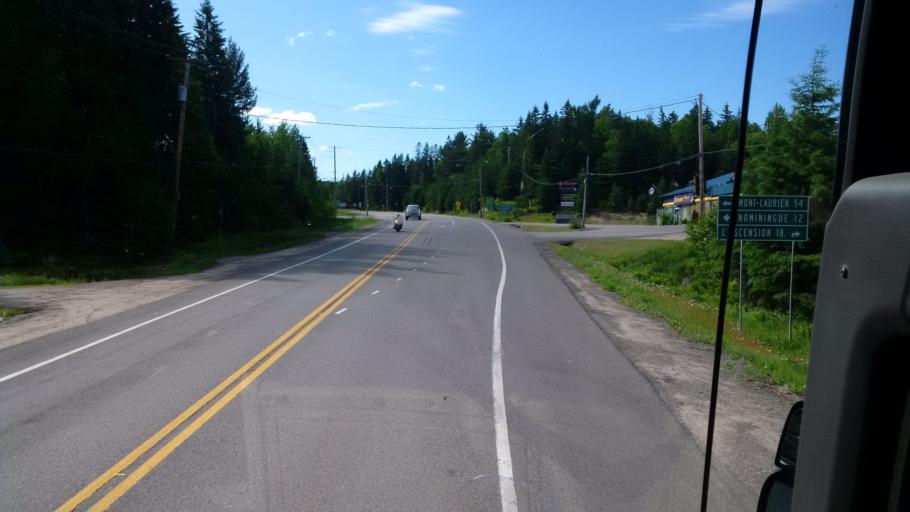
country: CA
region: Quebec
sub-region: Laurentides
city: Riviere-Rouge
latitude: 46.4340
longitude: -74.8983
